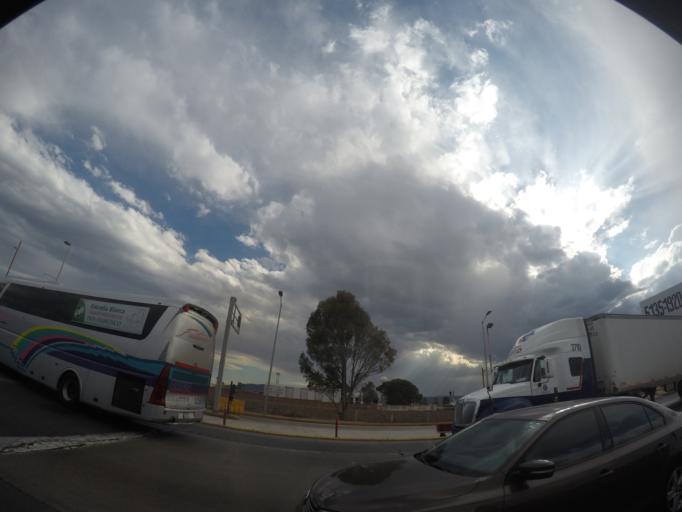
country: MX
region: Mexico
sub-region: Jilotepec
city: San Vicente (Calpulalpan Tercera Manzana)
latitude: 20.0747
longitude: -99.6124
